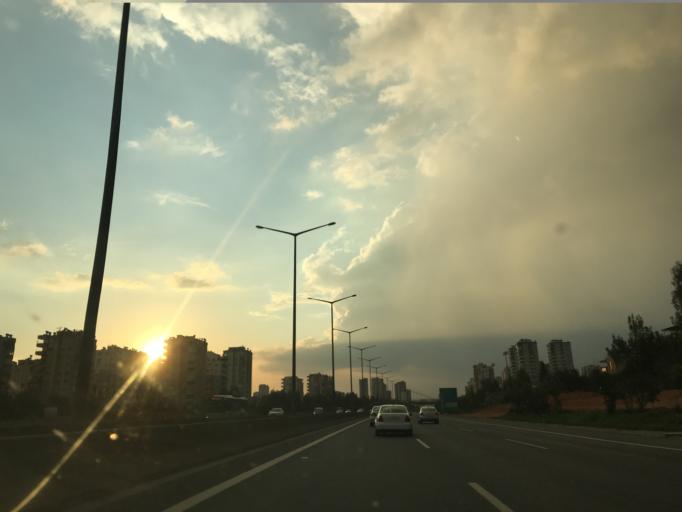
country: TR
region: Adana
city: Seyhan
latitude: 37.0303
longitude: 35.2717
